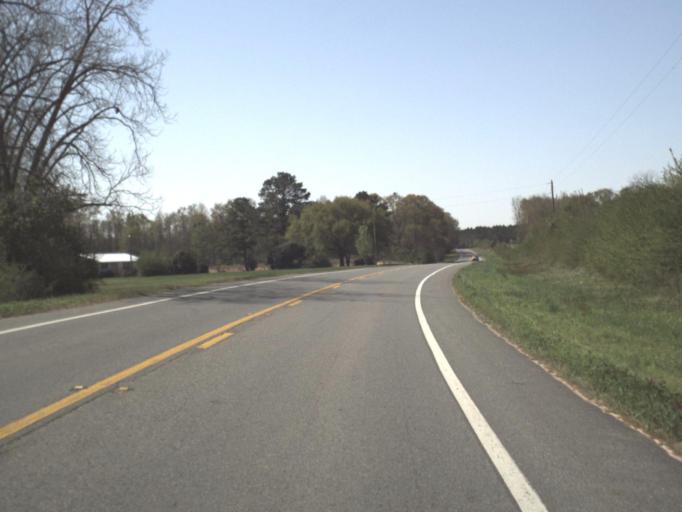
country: US
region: Florida
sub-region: Washington County
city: Chipley
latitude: 30.8616
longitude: -85.4942
